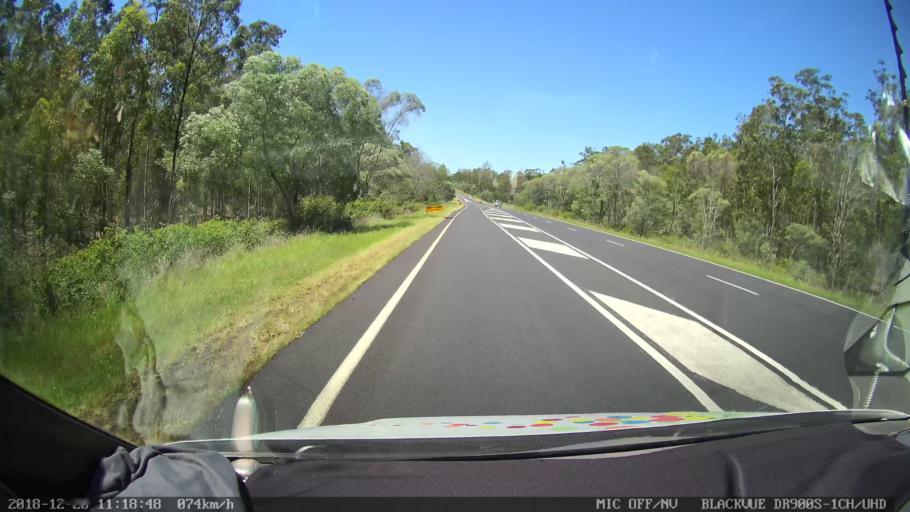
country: AU
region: New South Wales
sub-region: Richmond Valley
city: Casino
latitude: -29.0555
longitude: 153.0058
